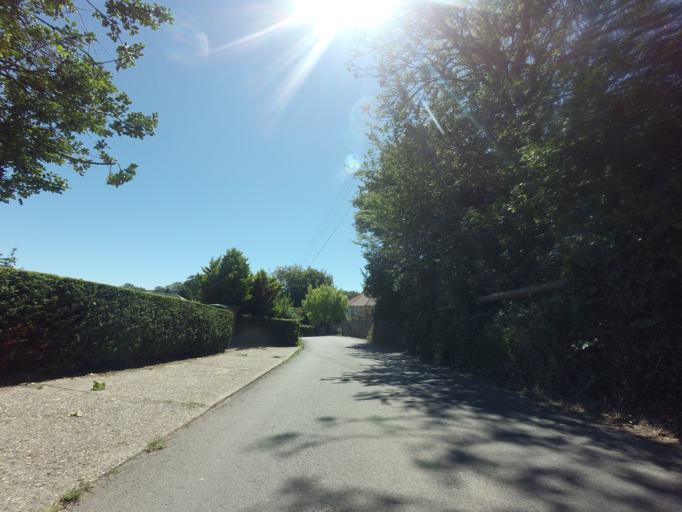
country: GB
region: England
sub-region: Kent
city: Eastry
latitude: 51.1994
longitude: 1.3149
